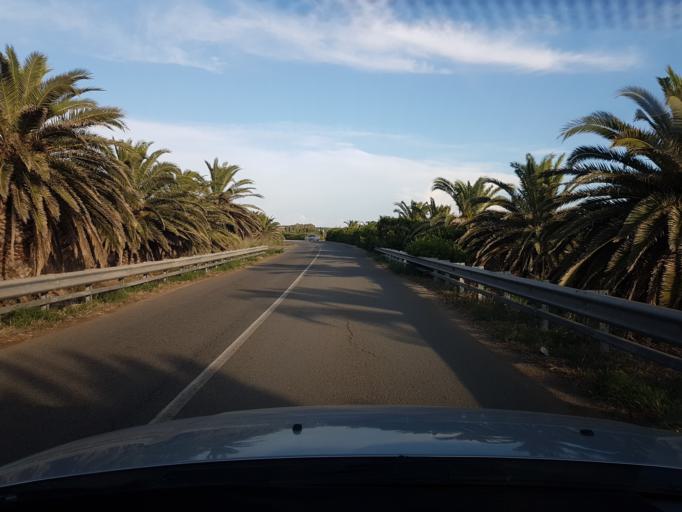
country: IT
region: Sardinia
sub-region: Provincia di Oristano
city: Cabras
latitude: 39.9507
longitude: 8.4105
